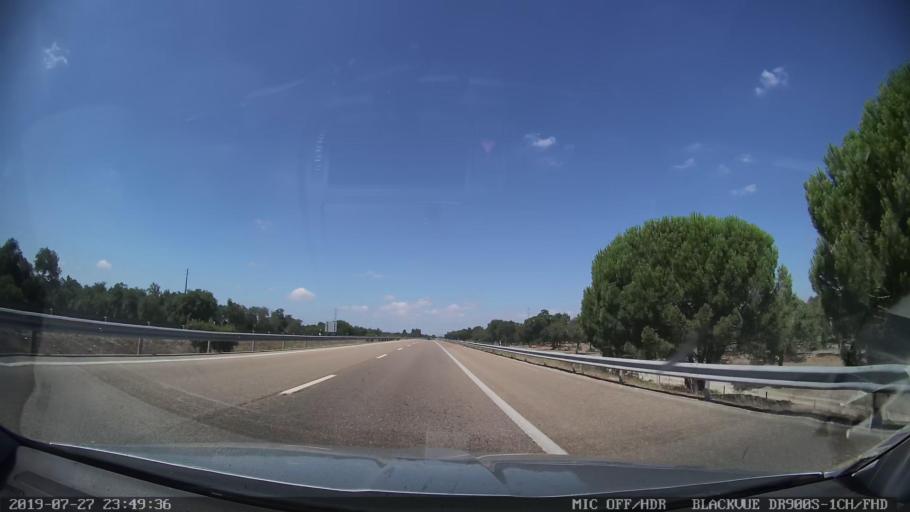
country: PT
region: Evora
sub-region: Vendas Novas
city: Vendas Novas
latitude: 38.6201
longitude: -8.5874
